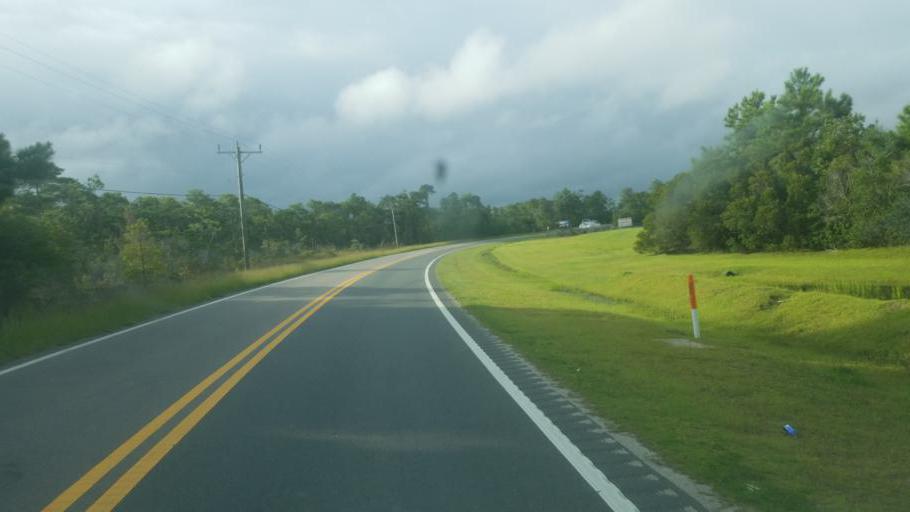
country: US
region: North Carolina
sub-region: Dare County
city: Manteo
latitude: 35.8877
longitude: -75.6591
